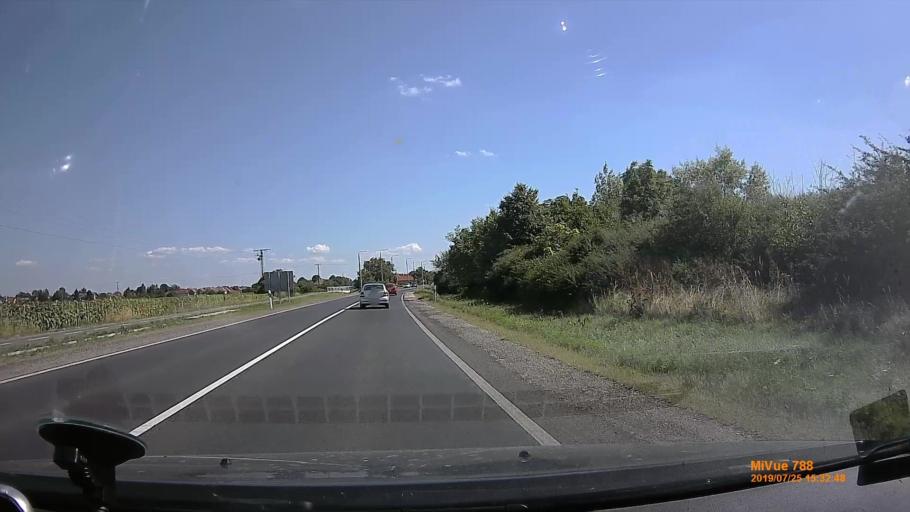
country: HU
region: Borsod-Abauj-Zemplen
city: Malyi
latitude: 48.0024
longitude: 20.8307
